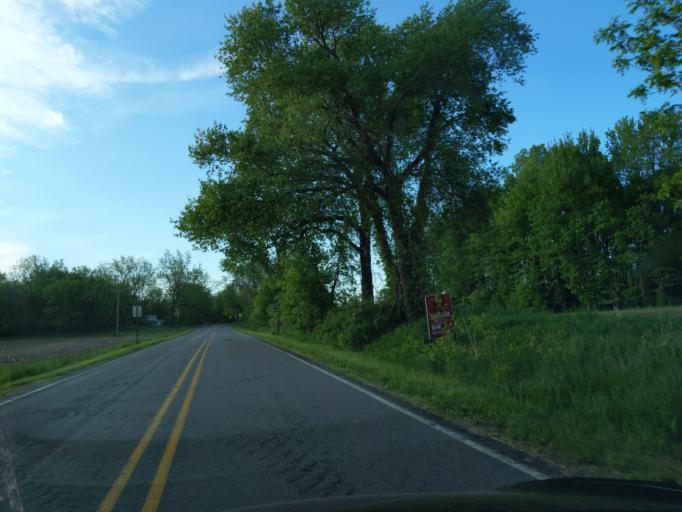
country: US
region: Michigan
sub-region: Ingham County
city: Leslie
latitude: 42.4596
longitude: -84.3140
